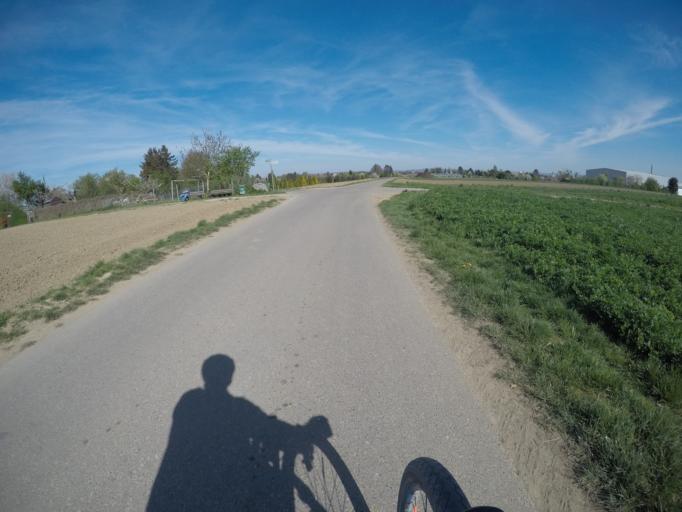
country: DE
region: Baden-Wuerttemberg
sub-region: Regierungsbezirk Stuttgart
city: Kornwestheim
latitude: 48.8685
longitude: 9.1671
